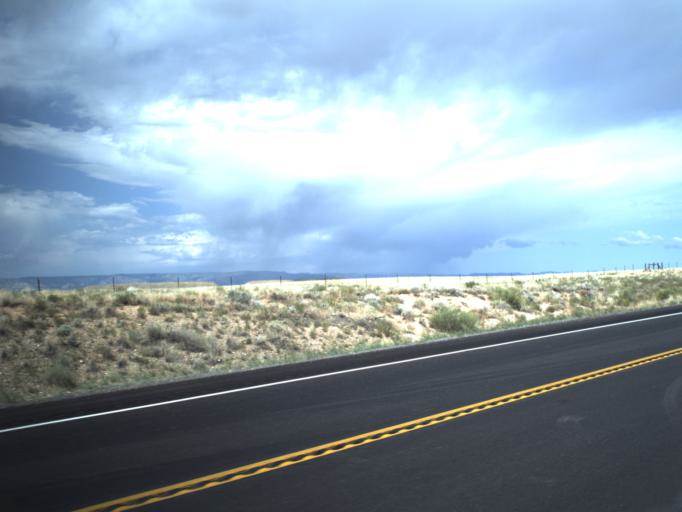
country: US
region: Utah
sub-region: Carbon County
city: East Carbon City
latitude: 39.4788
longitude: -110.5079
